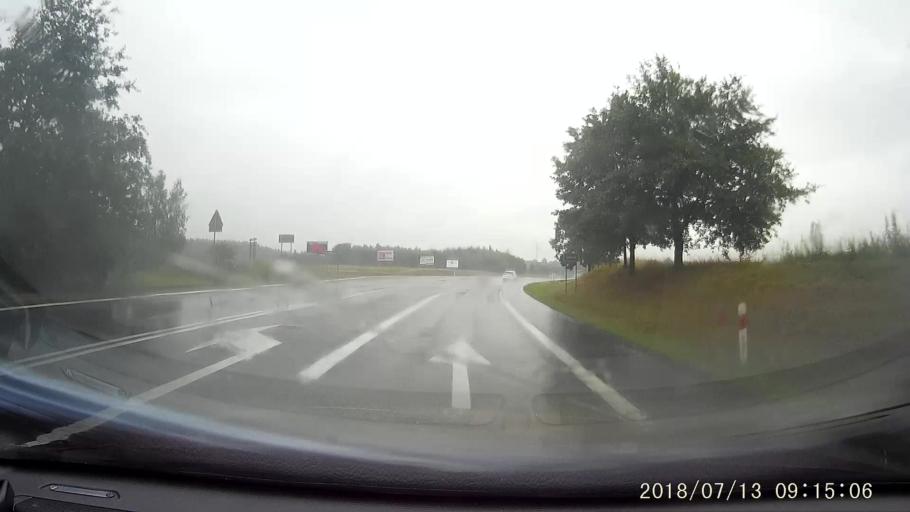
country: PL
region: Lower Silesian Voivodeship
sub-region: Powiat lubanski
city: Luban
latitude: 51.1334
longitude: 15.2668
